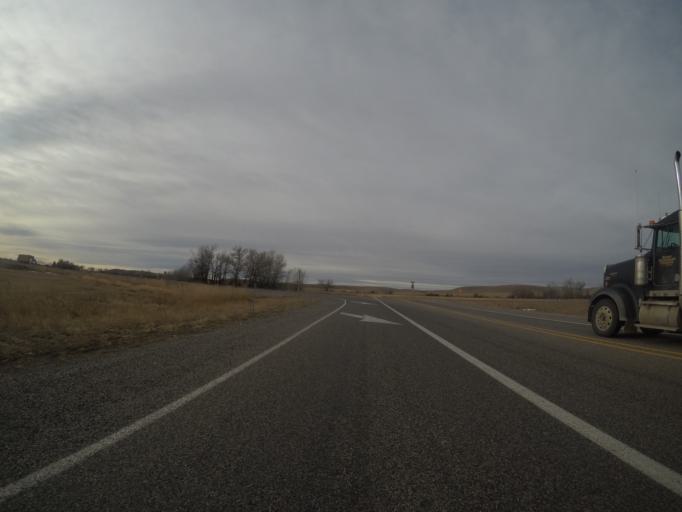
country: US
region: Montana
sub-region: Yellowstone County
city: Laurel
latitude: 45.5380
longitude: -108.8505
